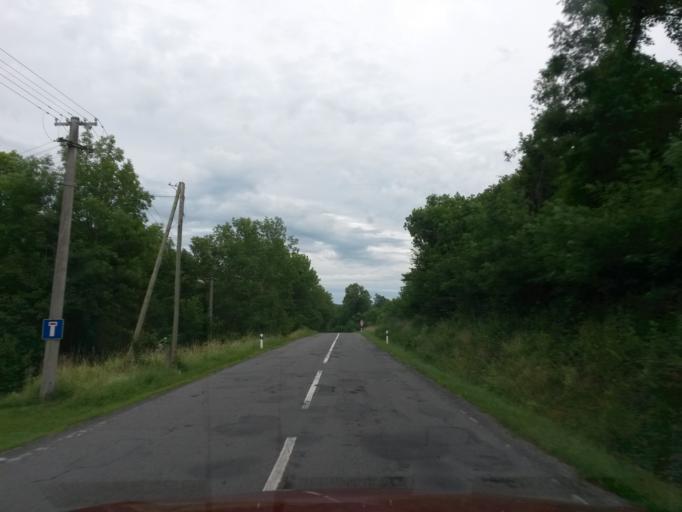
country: SK
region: Banskobystricky
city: Velky Krtis
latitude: 48.3803
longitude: 19.3863
